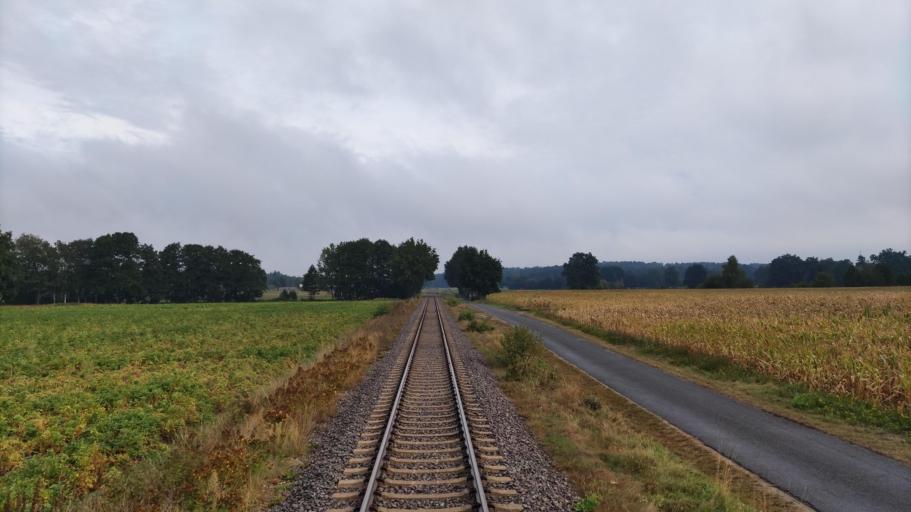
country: DE
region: Lower Saxony
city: Soltau
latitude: 52.9919
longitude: 9.8861
